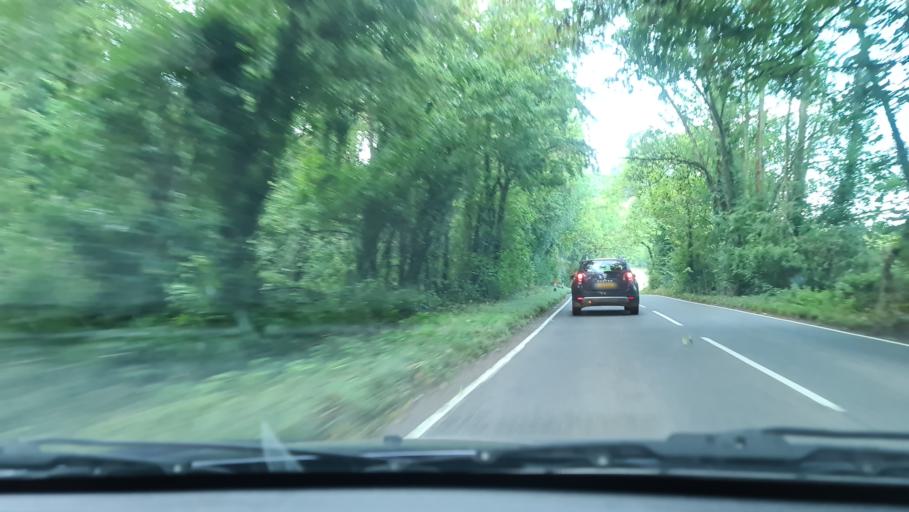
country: GB
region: England
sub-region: Hampshire
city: Romsey
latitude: 51.0498
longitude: -1.5172
